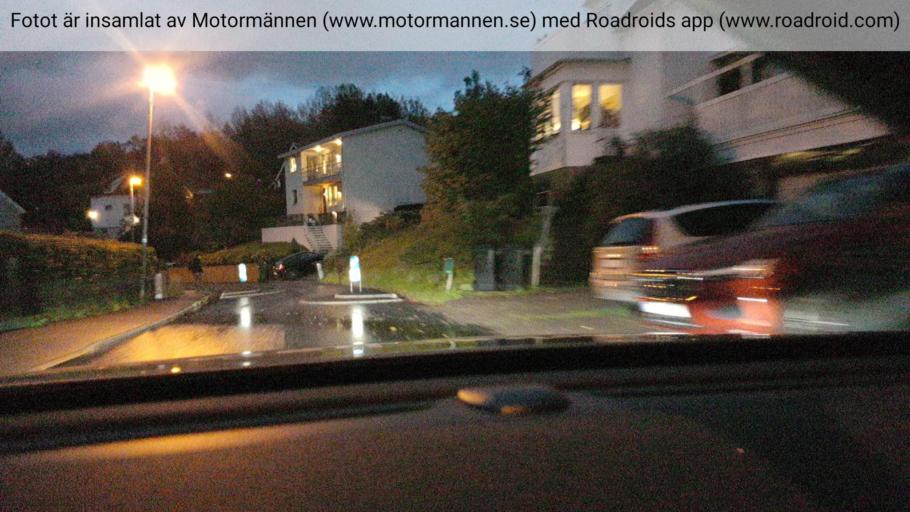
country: SE
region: Vaestra Goetaland
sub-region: Molndal
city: Moelndal
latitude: 57.6732
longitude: 11.9965
